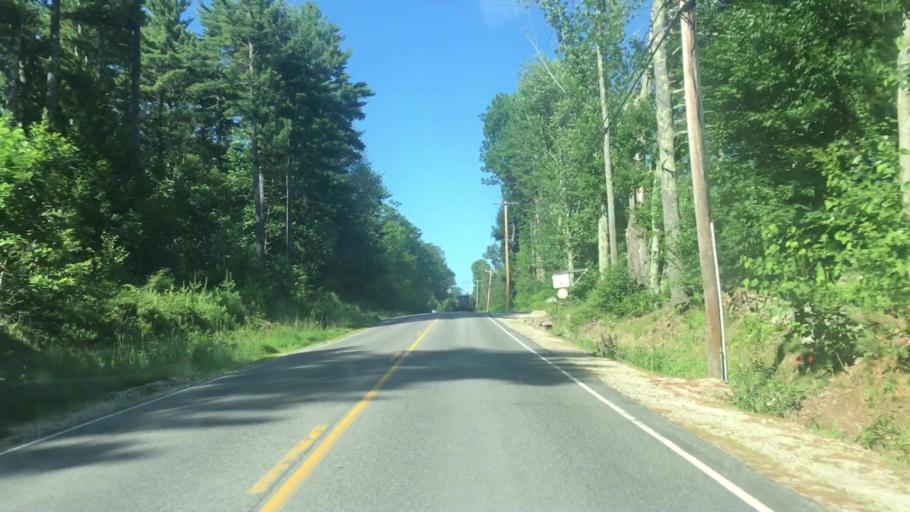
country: US
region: Maine
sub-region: York County
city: Buxton
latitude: 43.7077
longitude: -70.5754
